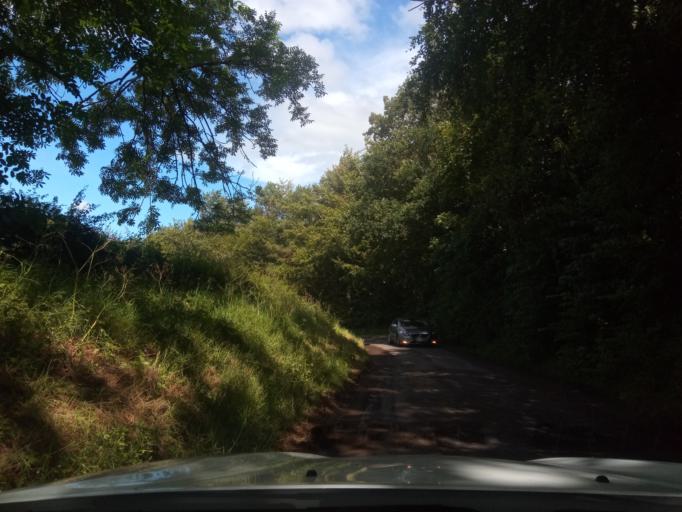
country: GB
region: Scotland
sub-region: The Scottish Borders
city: Saint Boswells
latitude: 55.5705
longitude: -2.5709
